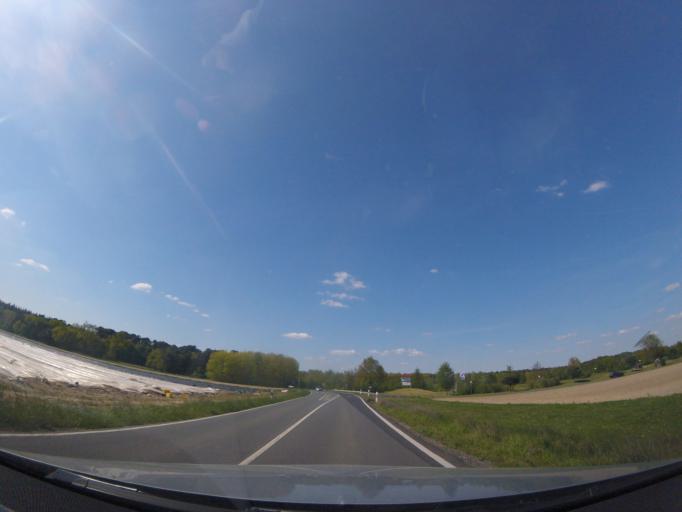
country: DE
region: Hesse
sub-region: Regierungsbezirk Darmstadt
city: Buttelborn
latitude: 49.9393
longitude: 8.5448
